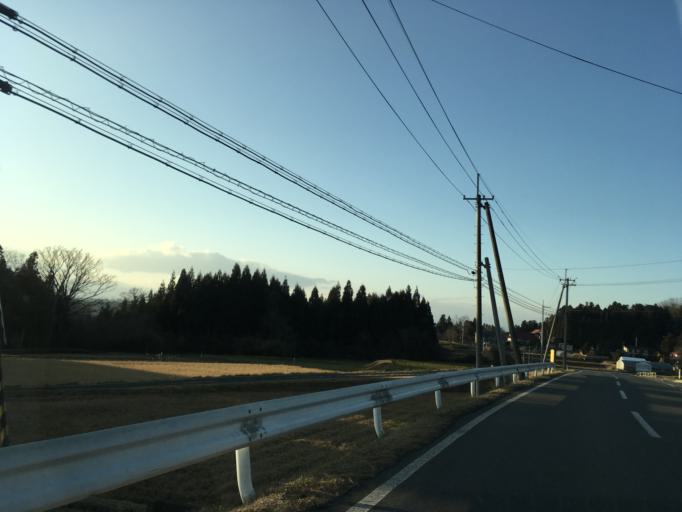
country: JP
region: Iwate
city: Ichinoseki
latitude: 38.8206
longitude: 141.2123
